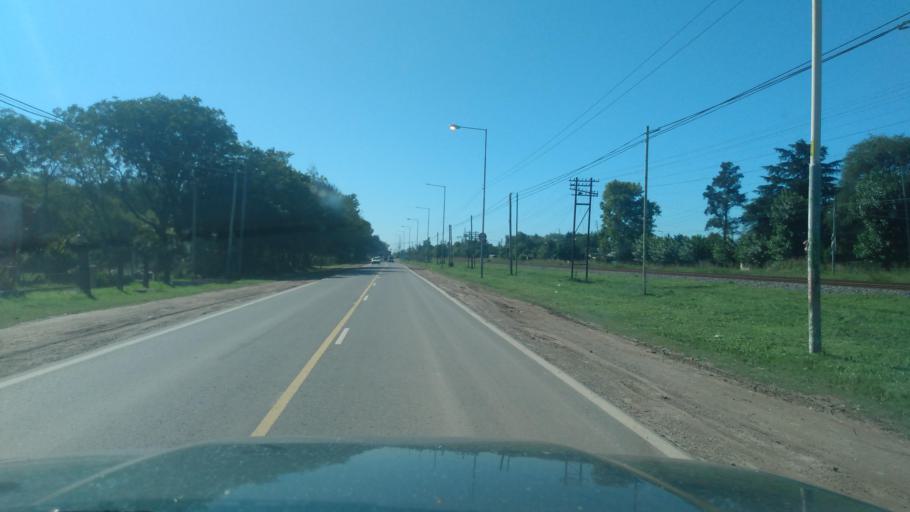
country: AR
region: Buenos Aires
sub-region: Partido de General Rodriguez
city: General Rodriguez
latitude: -34.5998
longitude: -58.9909
